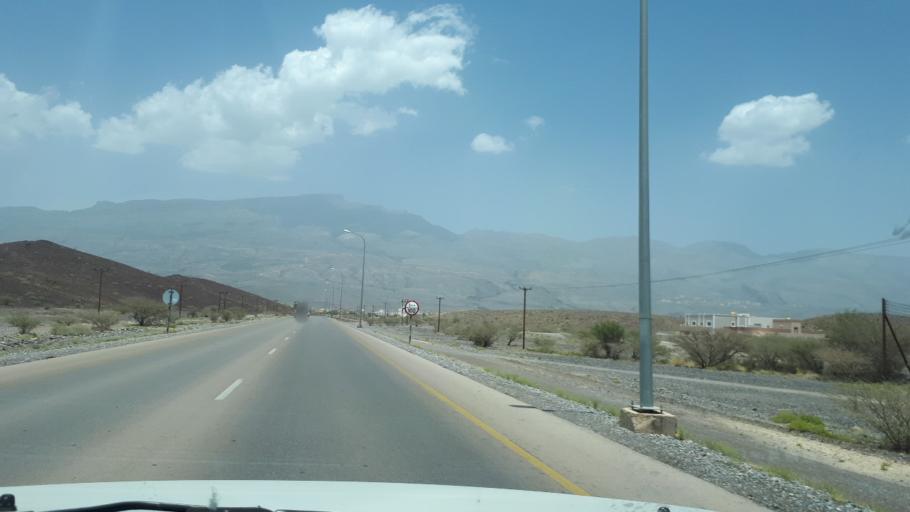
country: OM
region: Muhafazat ad Dakhiliyah
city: Bahla'
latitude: 23.0893
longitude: 57.2719
